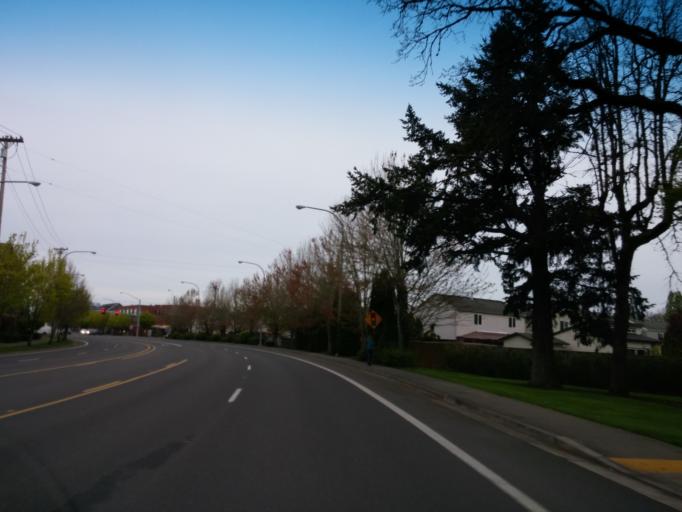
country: US
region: Oregon
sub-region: Washington County
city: Aloha
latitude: 45.5123
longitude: -122.8500
